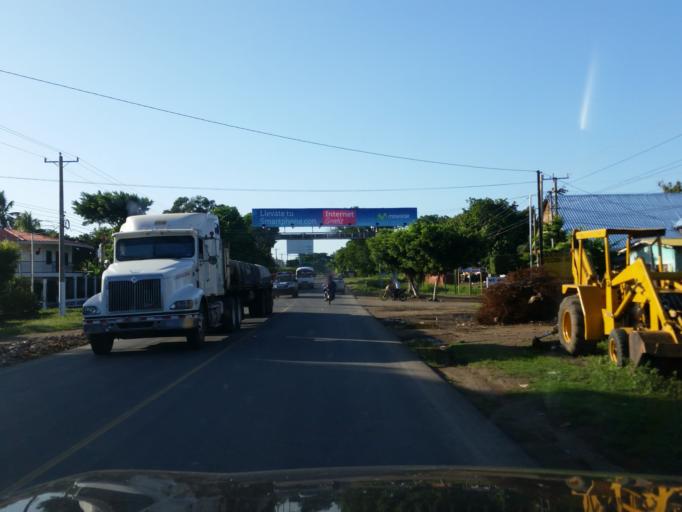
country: NI
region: Rivas
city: Rivas
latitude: 11.4499
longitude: -85.8334
